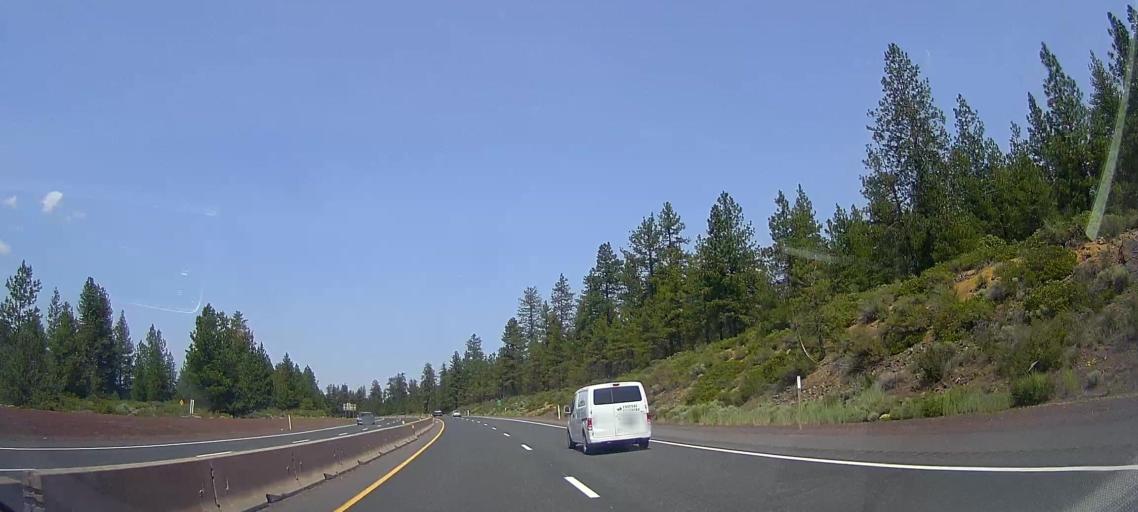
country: US
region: Oregon
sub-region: Deschutes County
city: Deschutes River Woods
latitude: 43.9137
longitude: -121.3502
